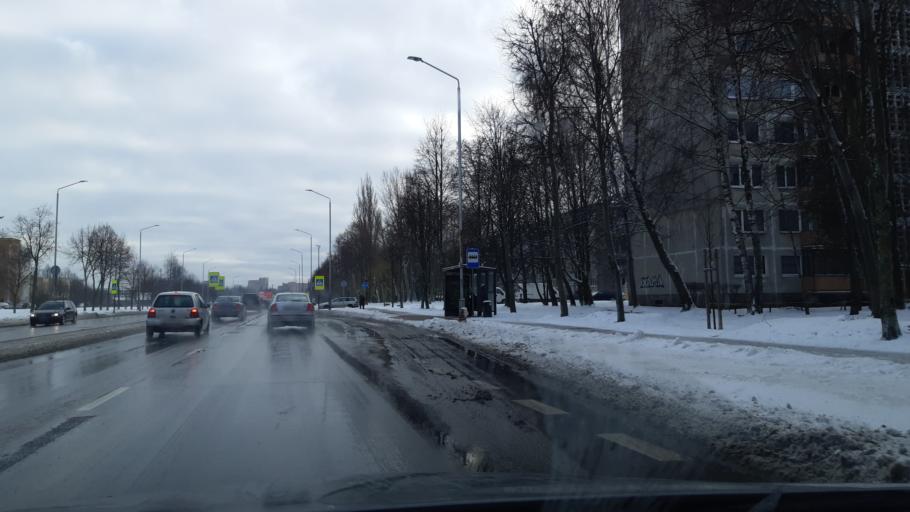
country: LT
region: Kauno apskritis
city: Dainava (Kaunas)
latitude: 54.9256
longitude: 23.9757
